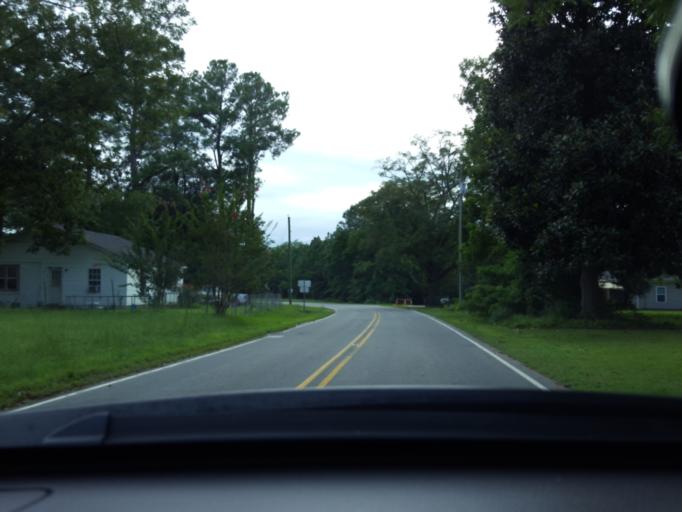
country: US
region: North Carolina
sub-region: Duplin County
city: Rose Hill
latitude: 34.8943
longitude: -78.0633
